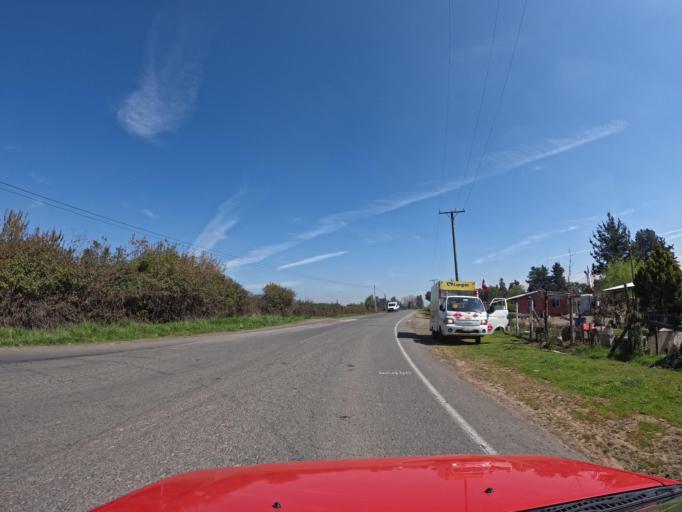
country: CL
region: Maule
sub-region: Provincia de Talca
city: San Clemente
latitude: -35.4841
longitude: -71.2720
